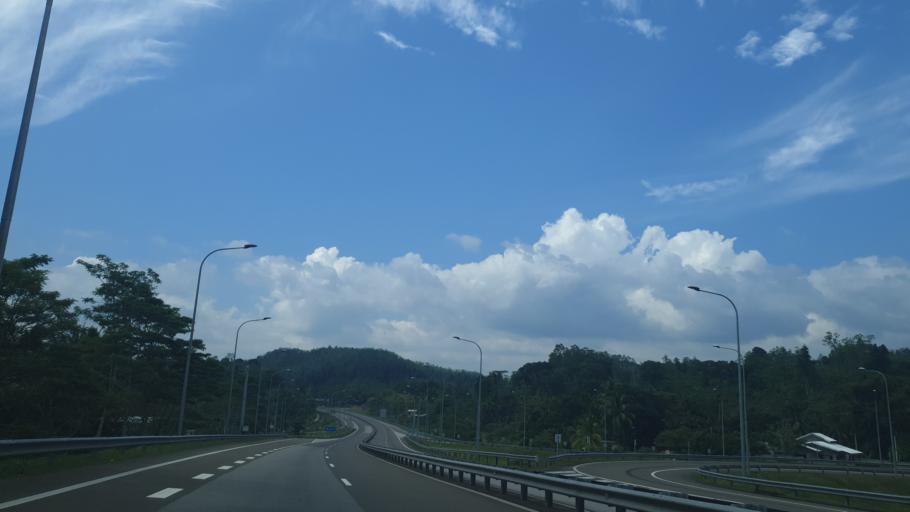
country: LK
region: Southern
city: Weligama
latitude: 6.0350
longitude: 80.3660
